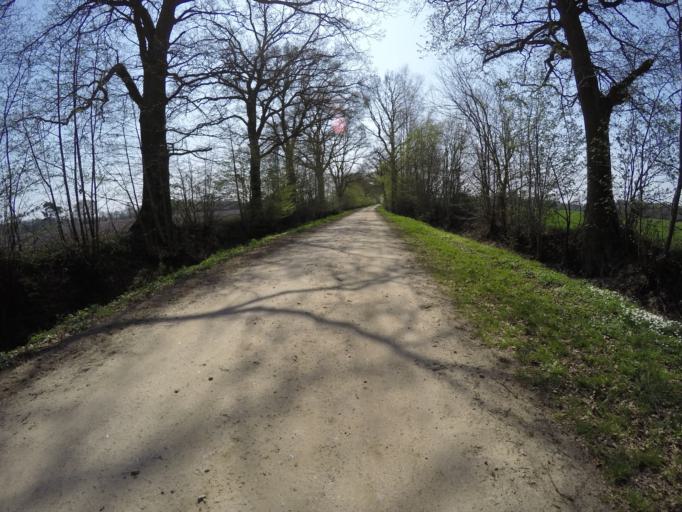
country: DE
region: Schleswig-Holstein
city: Borstel-Hohenraden
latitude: 53.7199
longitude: 9.8312
